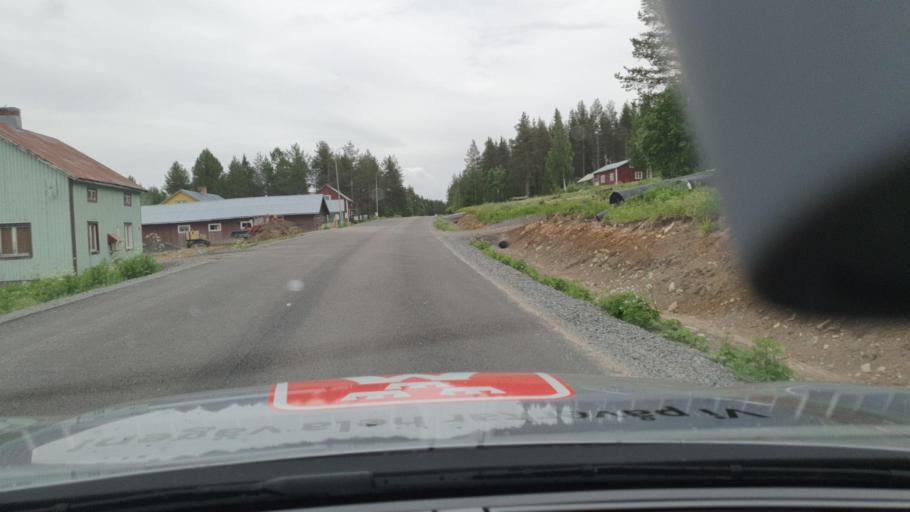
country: SE
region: Norrbotten
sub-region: Overtornea Kommun
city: OEvertornea
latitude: 66.6184
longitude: 23.2891
